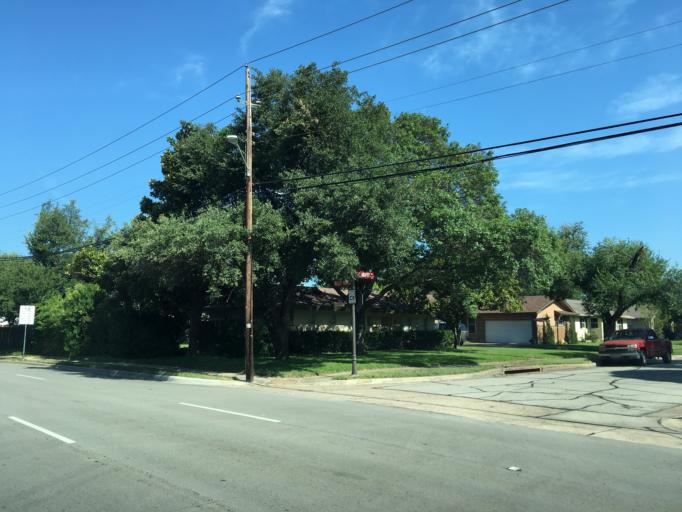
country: US
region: Texas
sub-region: Dallas County
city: Farmers Branch
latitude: 32.9243
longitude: -96.8693
